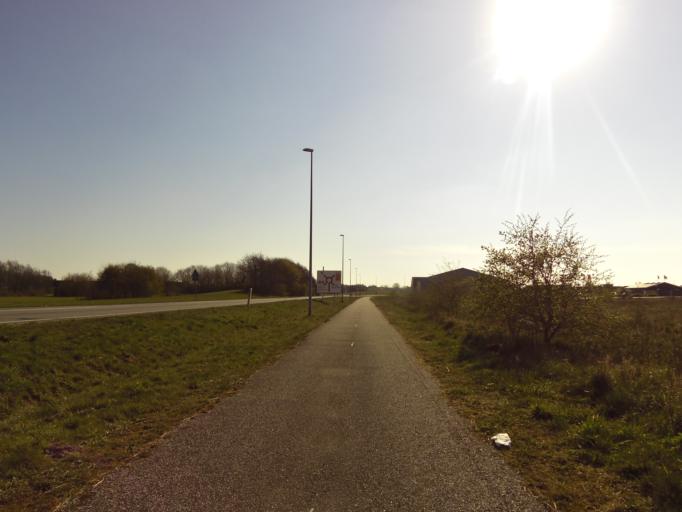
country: DK
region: South Denmark
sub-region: Esbjerg Kommune
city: Ribe
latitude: 55.3536
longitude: 8.7857
